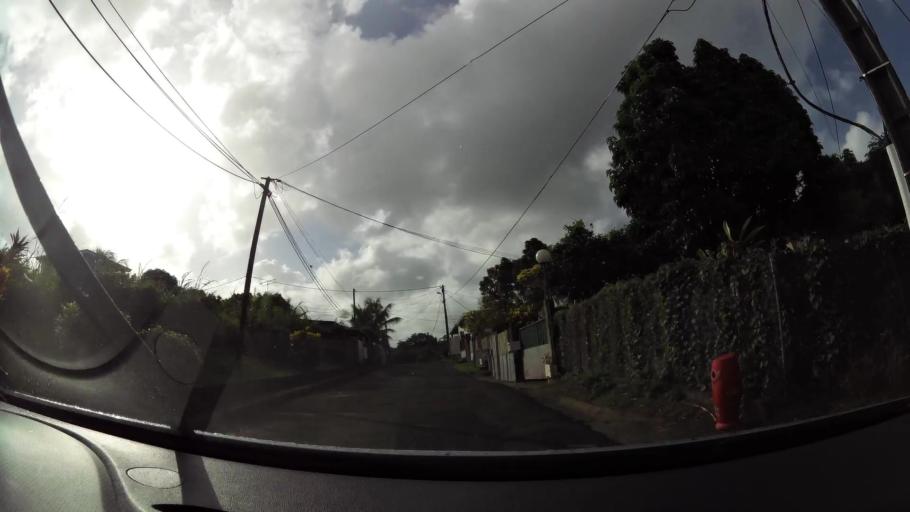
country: MQ
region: Martinique
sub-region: Martinique
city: Ducos
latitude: 14.5793
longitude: -60.9764
